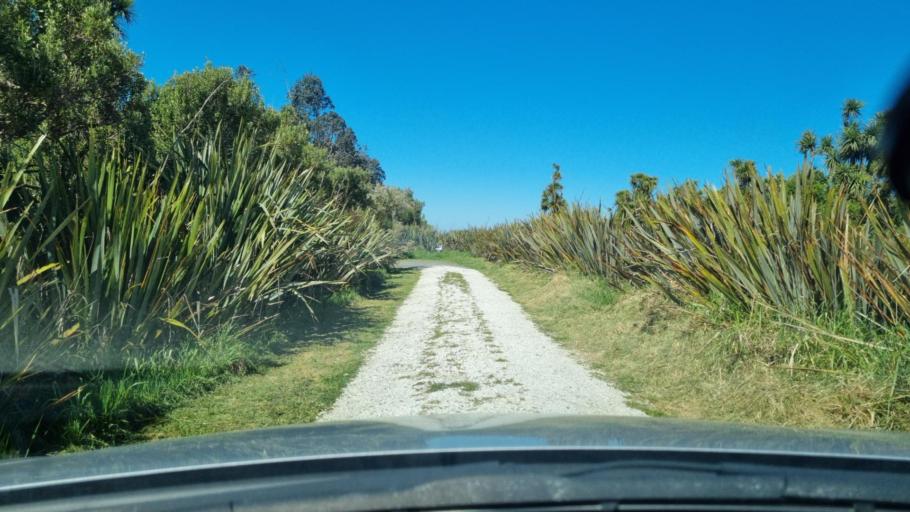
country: NZ
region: Southland
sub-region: Invercargill City
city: Invercargill
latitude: -46.4528
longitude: 168.3167
